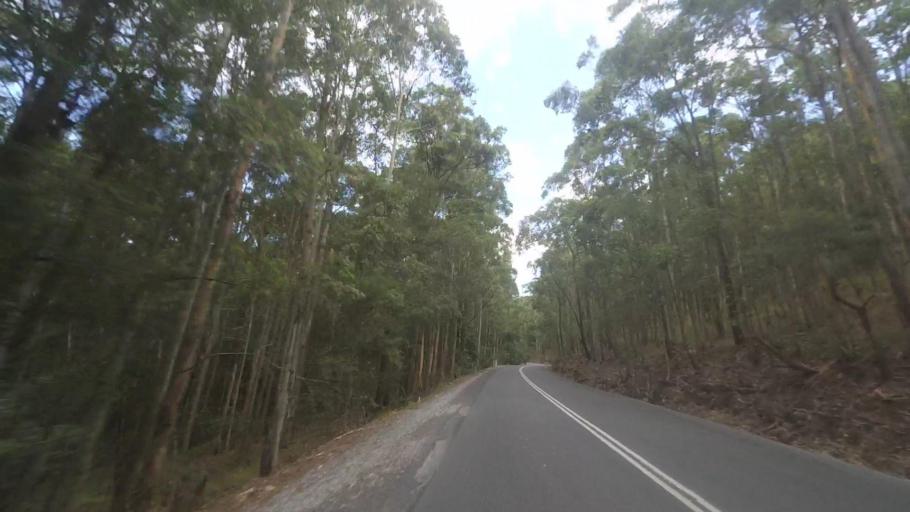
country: AU
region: New South Wales
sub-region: Great Lakes
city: Bulahdelah
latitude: -32.3909
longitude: 152.2436
